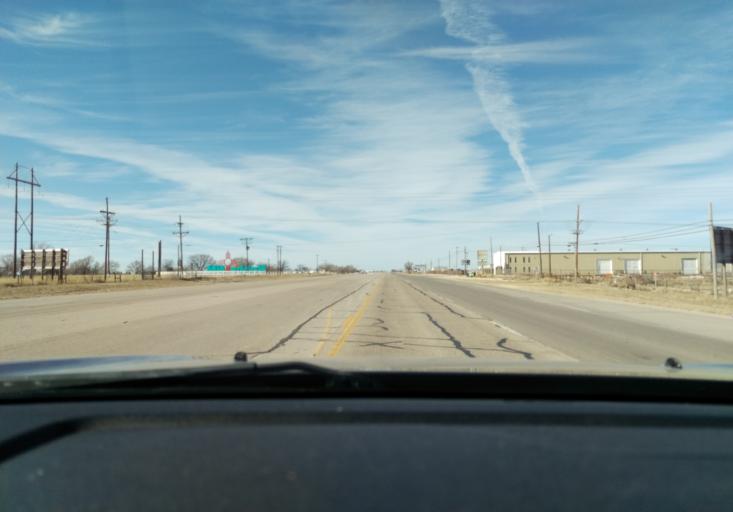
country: US
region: New Mexico
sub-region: Lea County
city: Hobbs
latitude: 32.6967
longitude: -103.1950
